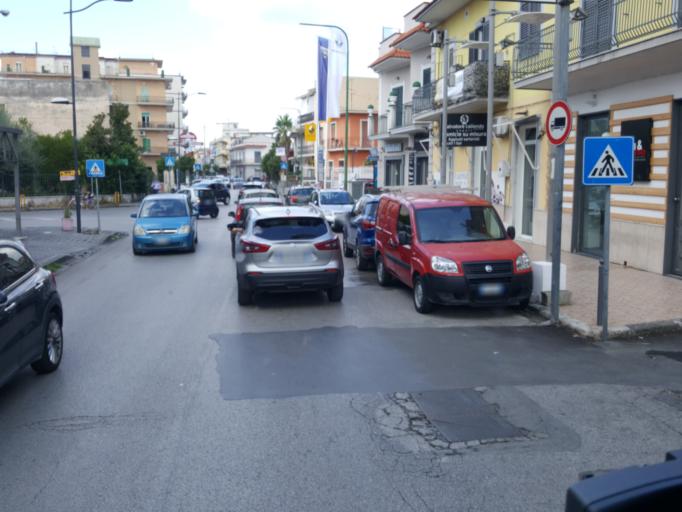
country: IT
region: Campania
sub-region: Provincia di Napoli
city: Nola
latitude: 40.9210
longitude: 14.5359
